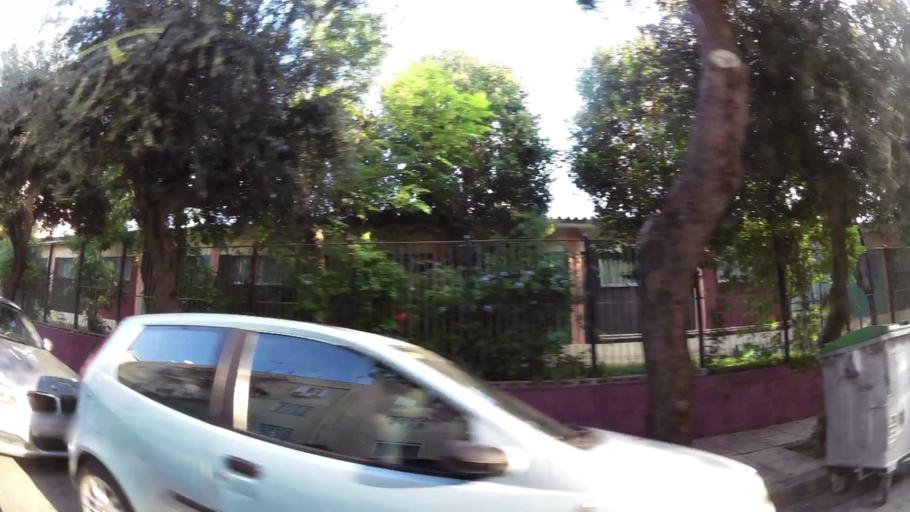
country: GR
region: Attica
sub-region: Nomarchia Athinas
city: Kallithea
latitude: 37.9531
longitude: 23.7075
